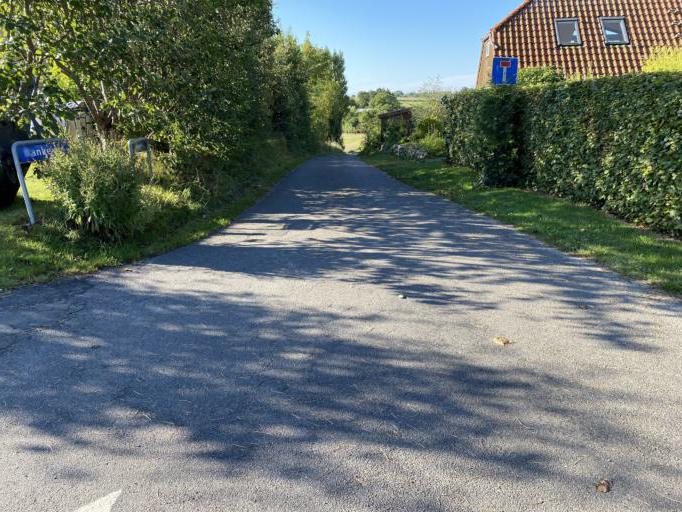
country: DK
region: Zealand
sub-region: Guldborgsund Kommune
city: Sakskobing
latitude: 54.9798
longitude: 11.5384
